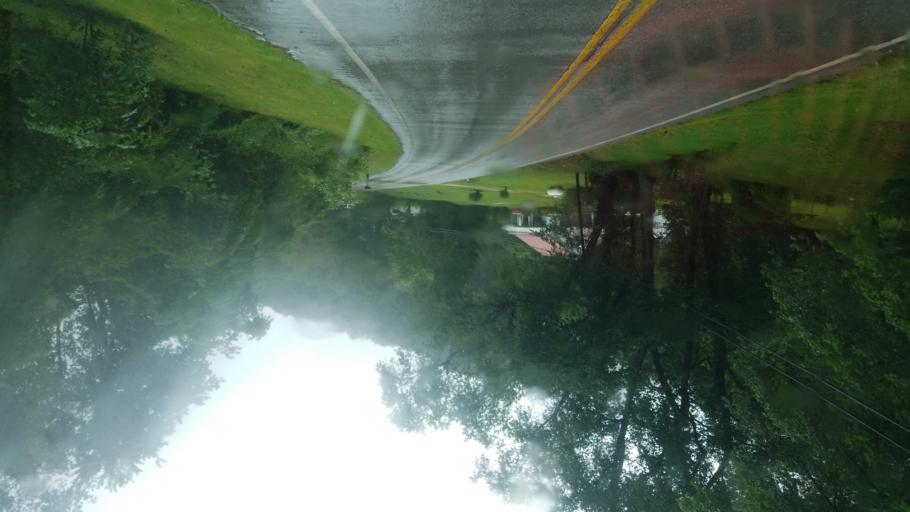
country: US
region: Kentucky
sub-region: Greenup County
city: South Shore
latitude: 38.6949
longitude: -82.9424
